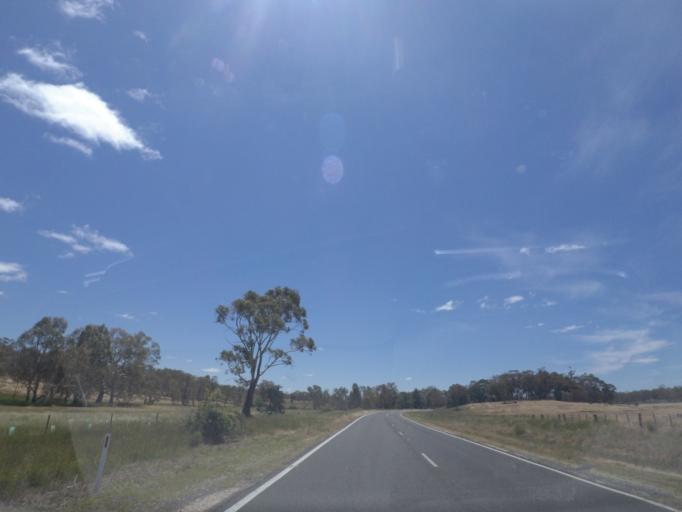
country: AU
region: Victoria
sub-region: Mount Alexander
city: Castlemaine
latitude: -37.1732
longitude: 144.1463
